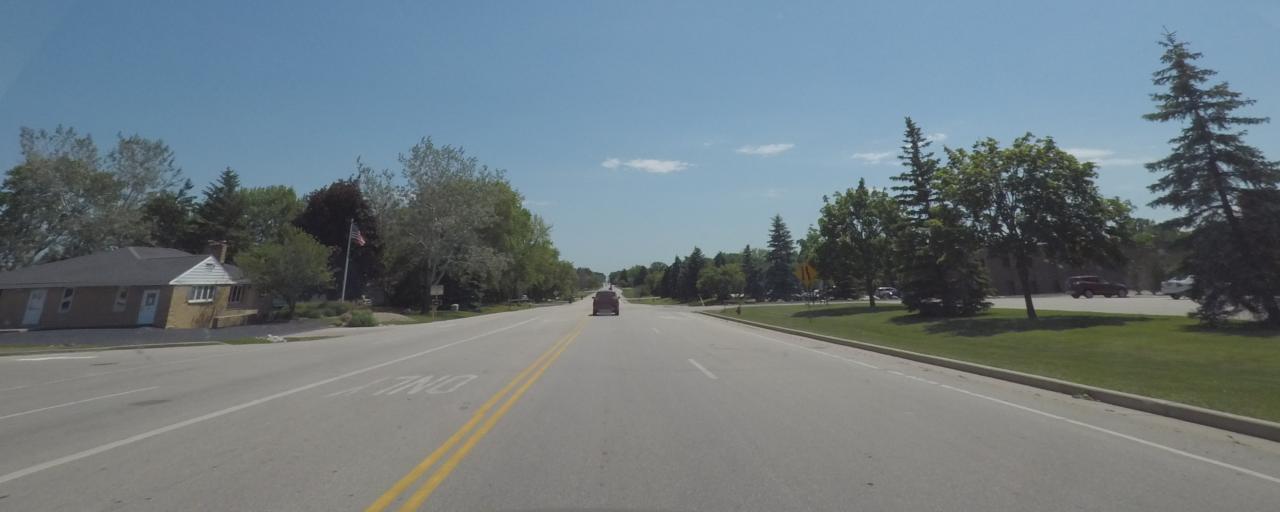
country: US
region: Wisconsin
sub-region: Waukesha County
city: New Berlin
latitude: 42.9936
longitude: -88.1280
